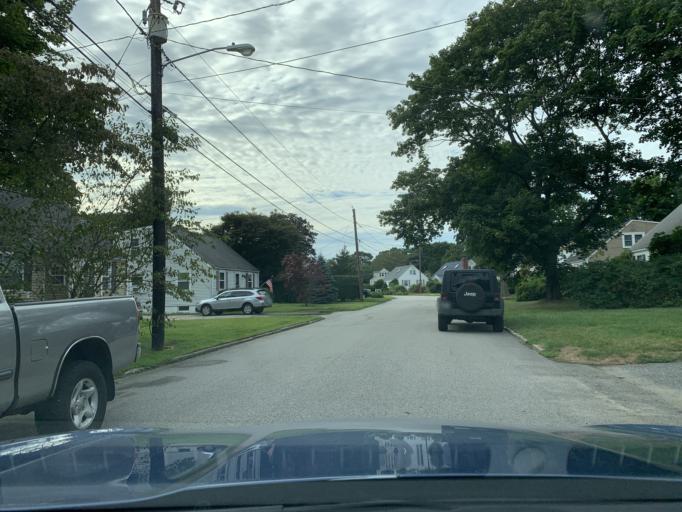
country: US
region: Rhode Island
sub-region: Kent County
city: East Greenwich
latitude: 41.6144
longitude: -71.4690
